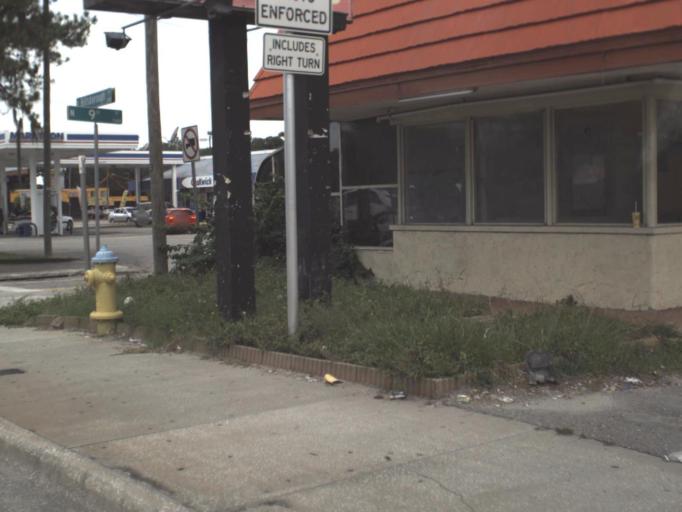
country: US
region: Florida
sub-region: Hillsborough County
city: Tampa
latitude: 27.9962
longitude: -82.4499
